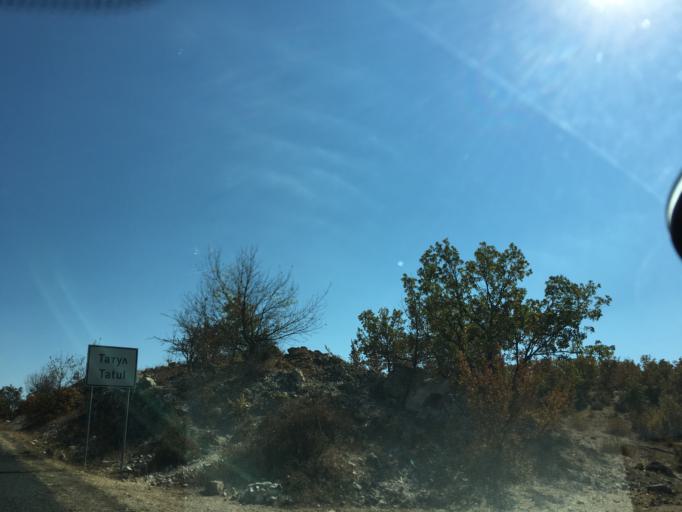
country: BG
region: Kurdzhali
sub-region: Obshtina Krumovgrad
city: Krumovgrad
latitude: 41.5461
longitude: 25.5454
